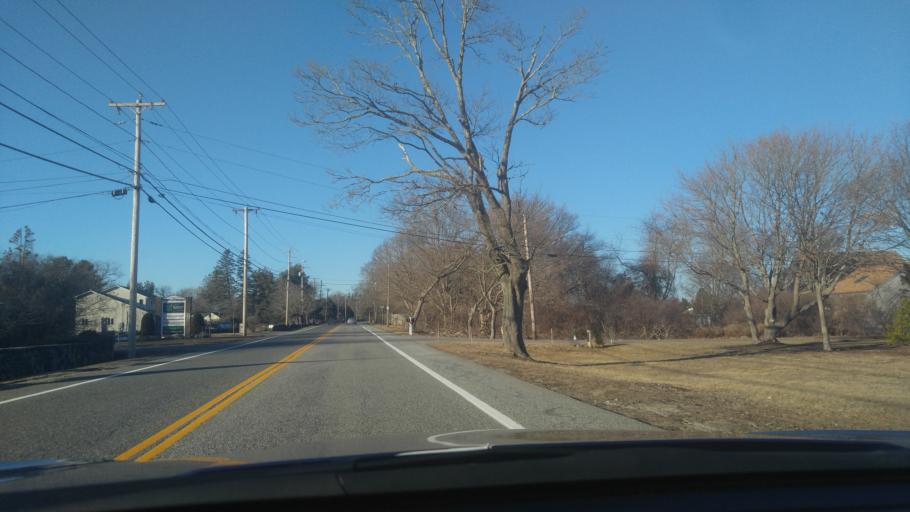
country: US
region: Rhode Island
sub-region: Washington County
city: Narragansett Pier
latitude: 41.4667
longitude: -71.4334
